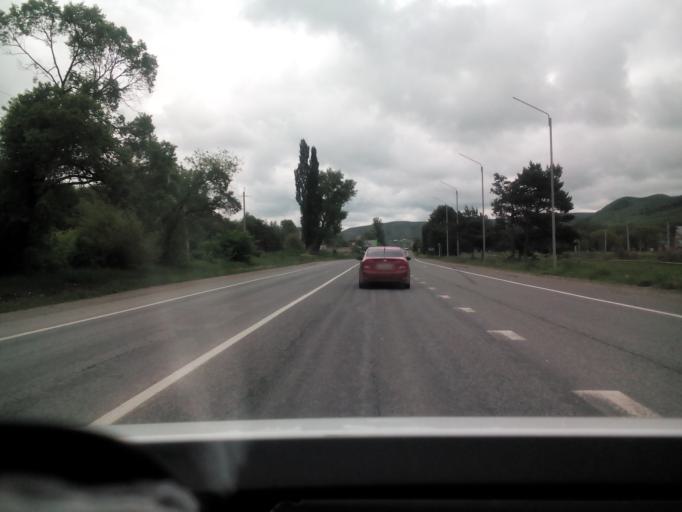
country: RU
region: Stavropol'skiy
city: Kislovodsk
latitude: 43.9587
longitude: 42.7641
